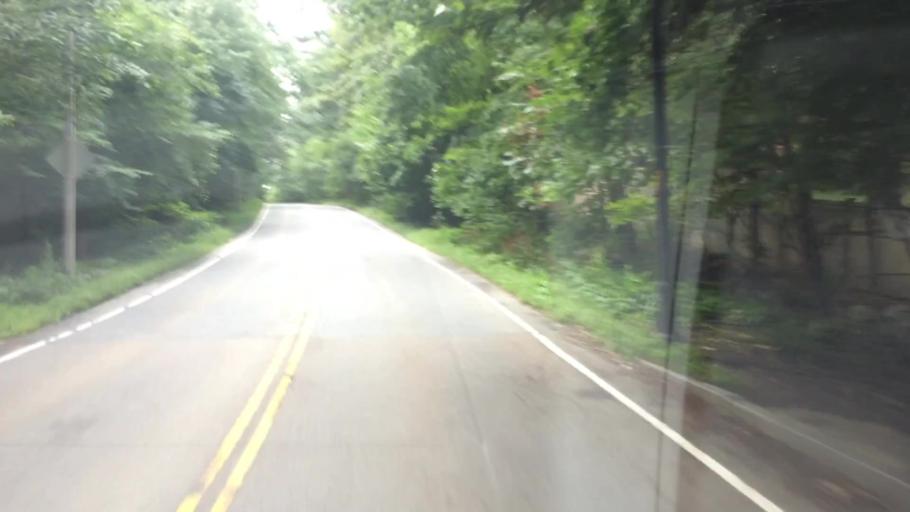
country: US
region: Massachusetts
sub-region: Middlesex County
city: Winchester
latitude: 42.4478
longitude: -71.1256
